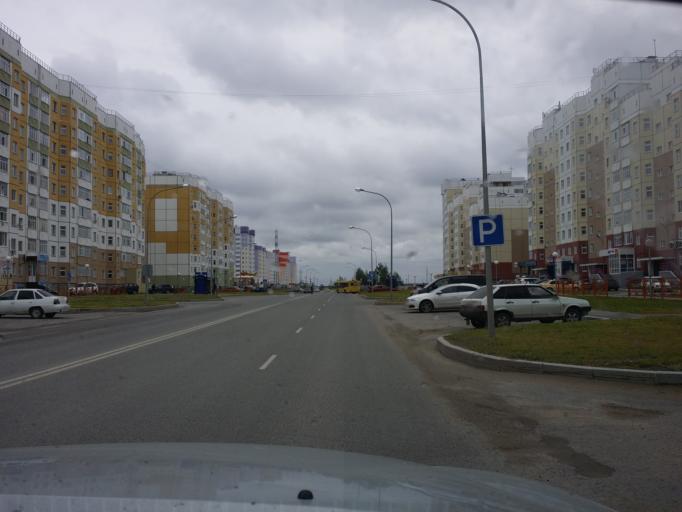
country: RU
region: Khanty-Mansiyskiy Avtonomnyy Okrug
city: Nizhnevartovsk
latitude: 60.9333
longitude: 76.6169
